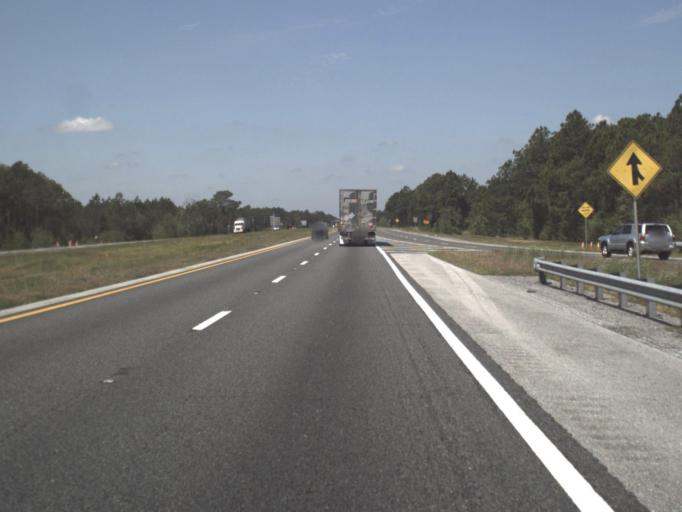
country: US
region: Florida
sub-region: Santa Rosa County
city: Bagdad
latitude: 30.5341
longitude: -87.0903
